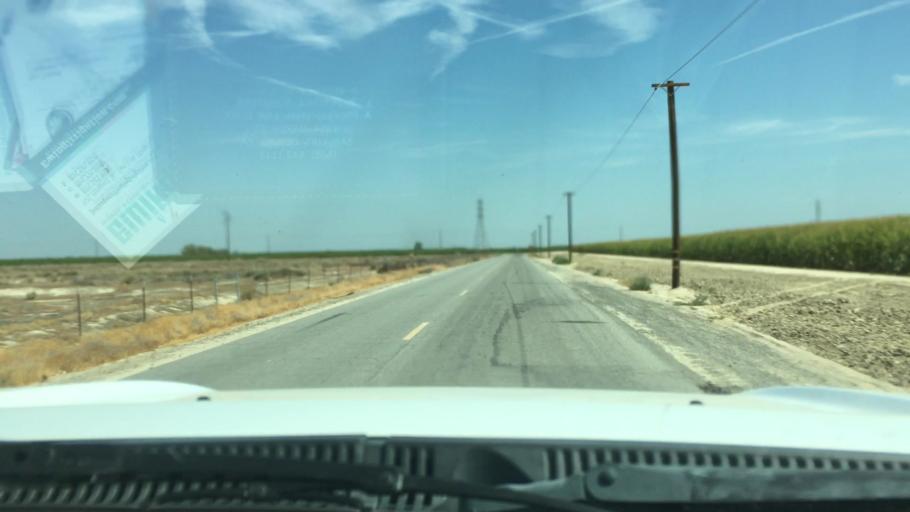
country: US
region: California
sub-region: Kern County
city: Buttonwillow
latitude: 35.4383
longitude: -119.3760
